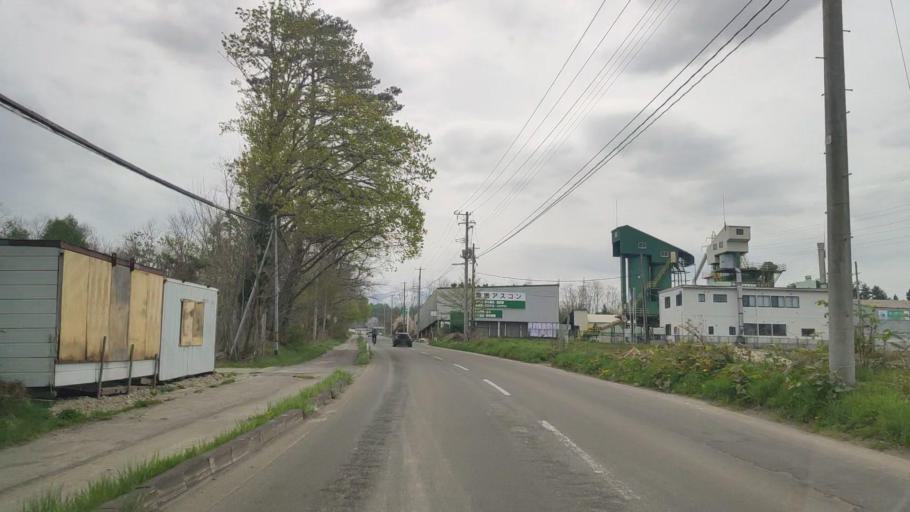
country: JP
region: Aomori
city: Aomori Shi
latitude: 40.7740
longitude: 140.7964
